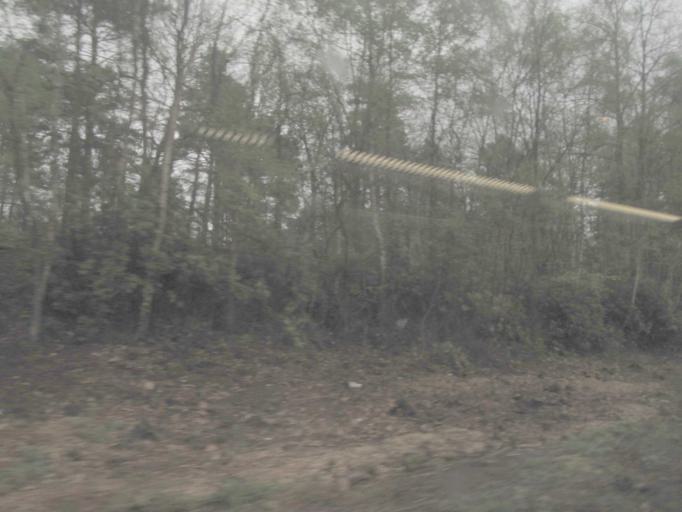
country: GB
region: England
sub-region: Hampshire
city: Yateley
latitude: 51.3628
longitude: -0.8170
